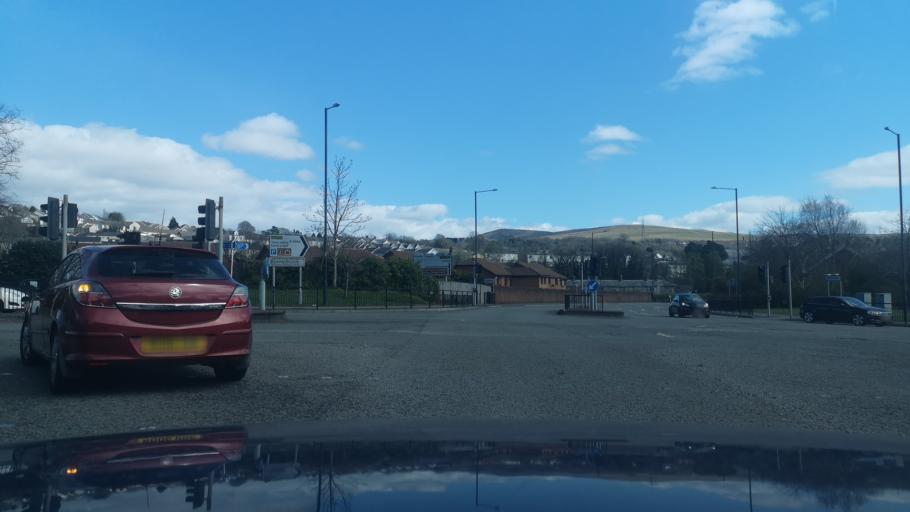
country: GB
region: Wales
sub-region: Merthyr Tydfil County Borough
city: Merthyr Tydfil
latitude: 51.7505
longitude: -3.3885
